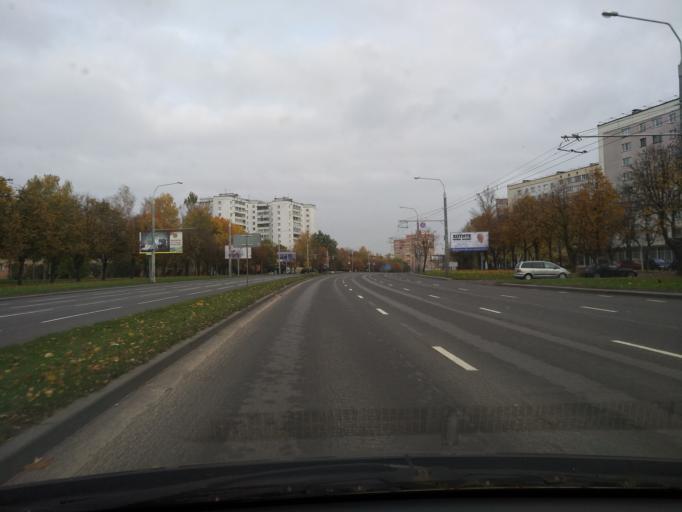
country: BY
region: Minsk
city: Novoye Medvezhino
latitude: 53.9164
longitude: 27.4951
